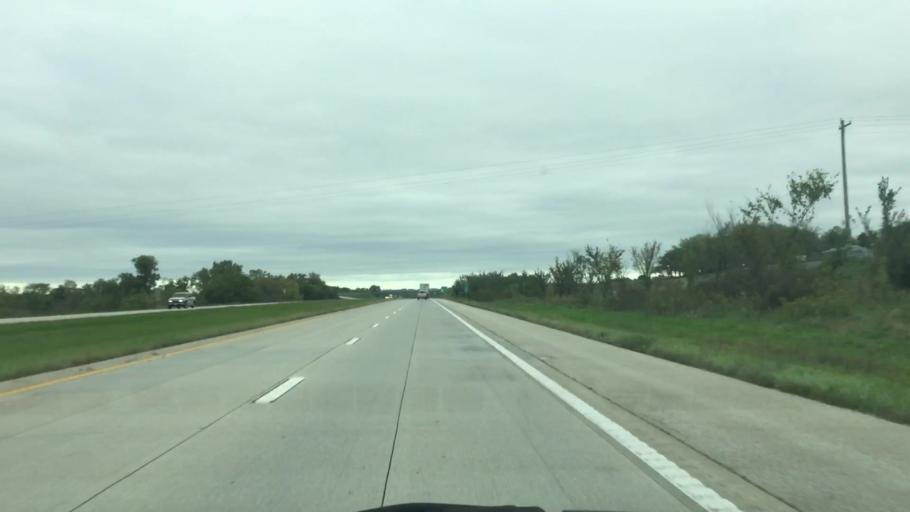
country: US
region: Missouri
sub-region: Daviess County
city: Gallatin
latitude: 39.9882
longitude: -94.0949
